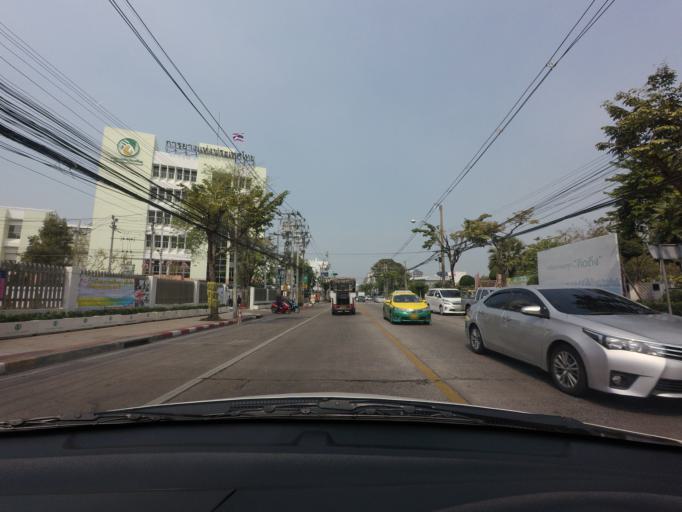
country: TH
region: Bangkok
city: Taling Chan
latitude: 13.7713
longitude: 100.4682
